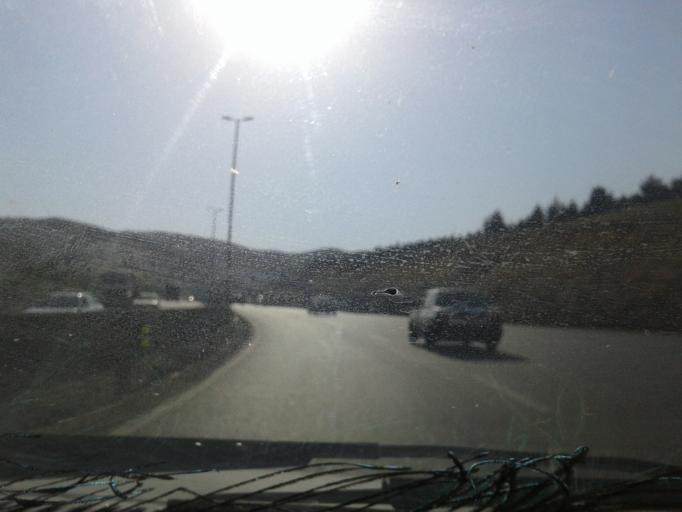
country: IR
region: Tehran
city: Pakdasht
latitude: 35.7322
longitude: 51.6874
